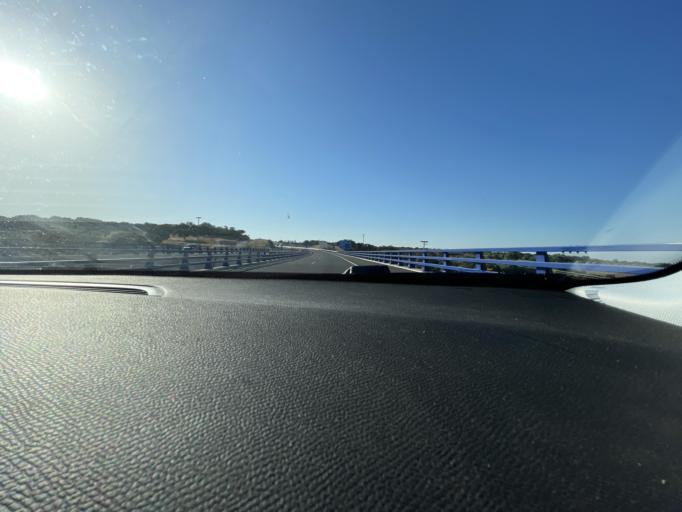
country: ES
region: Castille and Leon
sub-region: Provincia de Salamanca
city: Fuentes de Onoro
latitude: 40.5968
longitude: -6.8083
